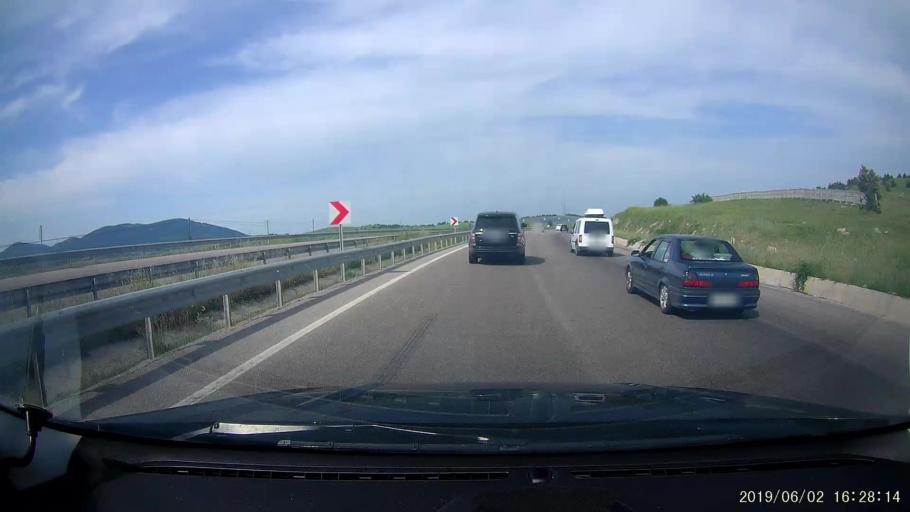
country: TR
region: Samsun
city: Ladik
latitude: 41.0065
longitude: 35.8427
